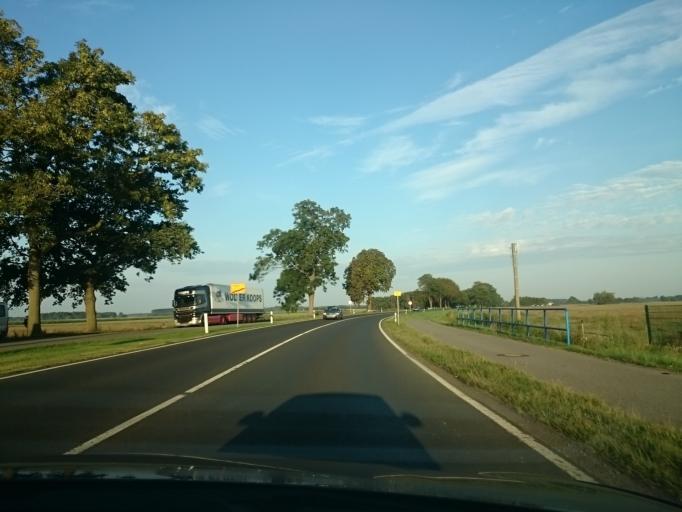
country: DE
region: Mecklenburg-Vorpommern
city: Ostseebad Zinnowitz
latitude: 54.0679
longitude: 13.8986
